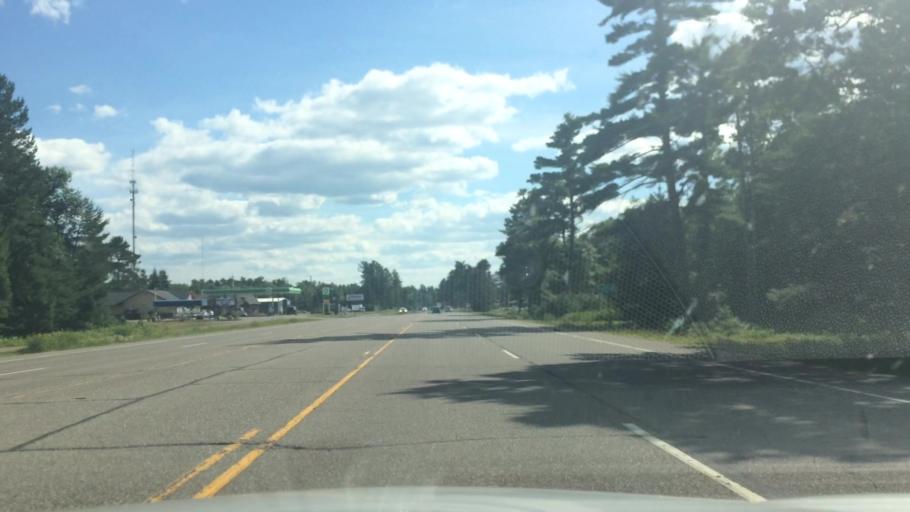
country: US
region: Wisconsin
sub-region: Vilas County
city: Lac du Flambeau
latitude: 45.8270
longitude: -89.7198
